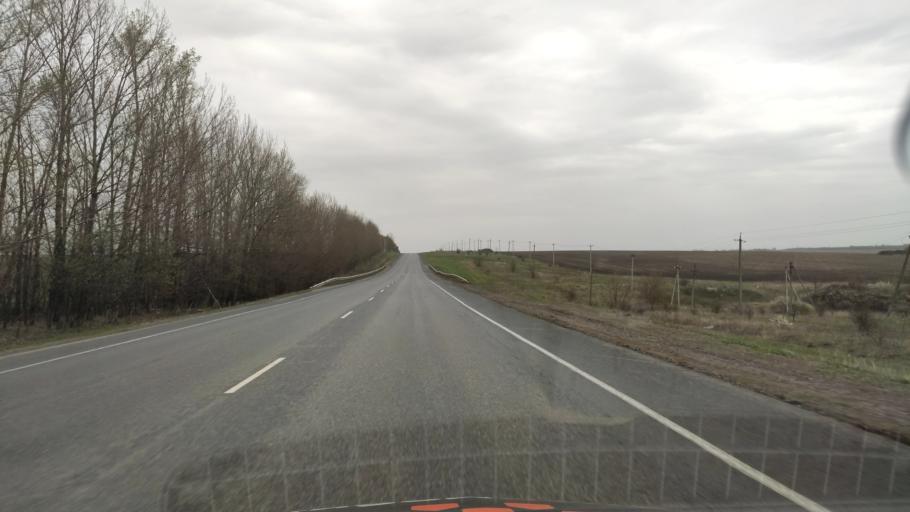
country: RU
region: Kursk
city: Gorshechnoye
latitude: 51.4997
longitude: 37.9827
